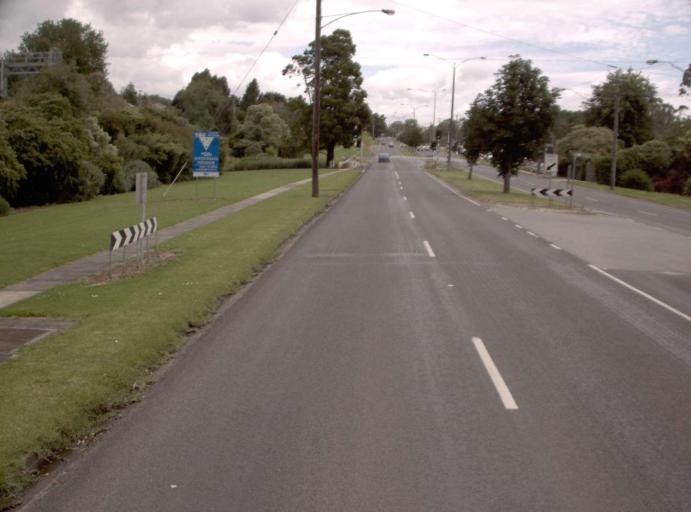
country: AU
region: Victoria
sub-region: Baw Baw
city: Warragul
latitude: -38.1608
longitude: 145.9241
